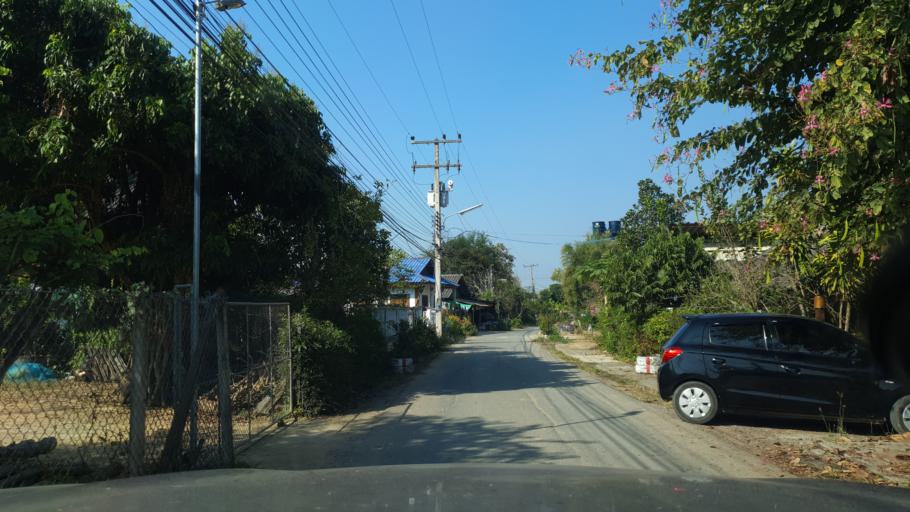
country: TH
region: Lamphun
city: Ban Thi
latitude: 18.6855
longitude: 99.1007
